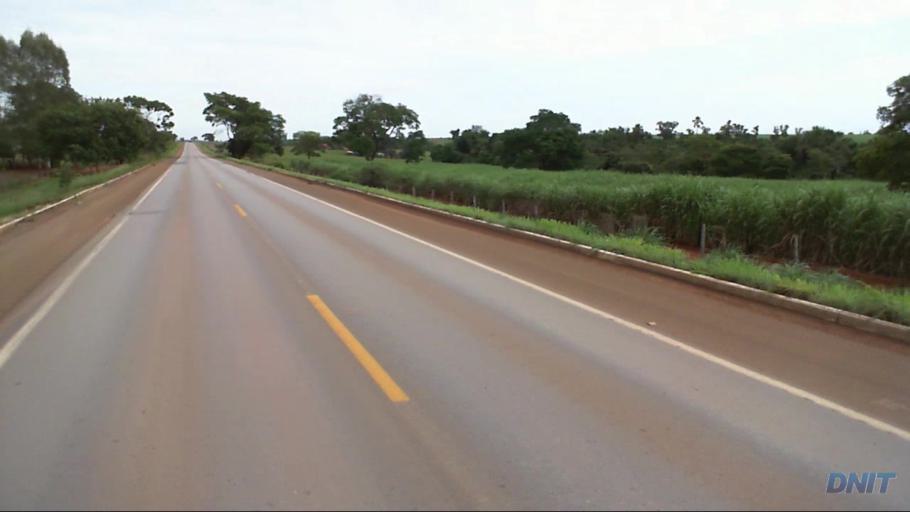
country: BR
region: Goias
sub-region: Uruacu
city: Uruacu
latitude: -14.7120
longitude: -49.1082
